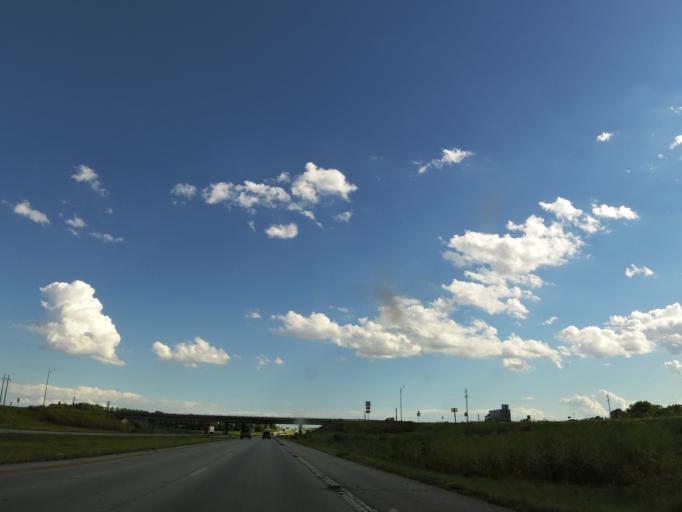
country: US
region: Illinois
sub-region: Adams County
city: Quincy
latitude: 39.9192
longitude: -91.5243
